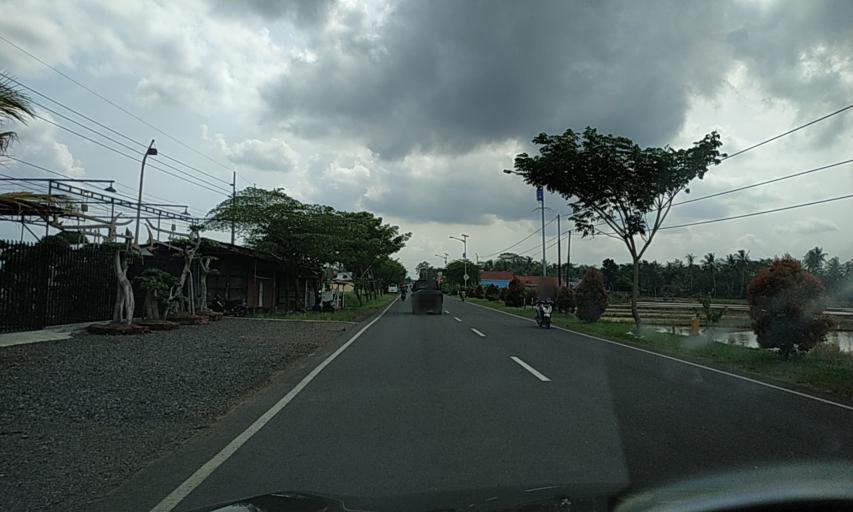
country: ID
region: Central Java
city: Sogati
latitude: -7.3342
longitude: 108.6777
